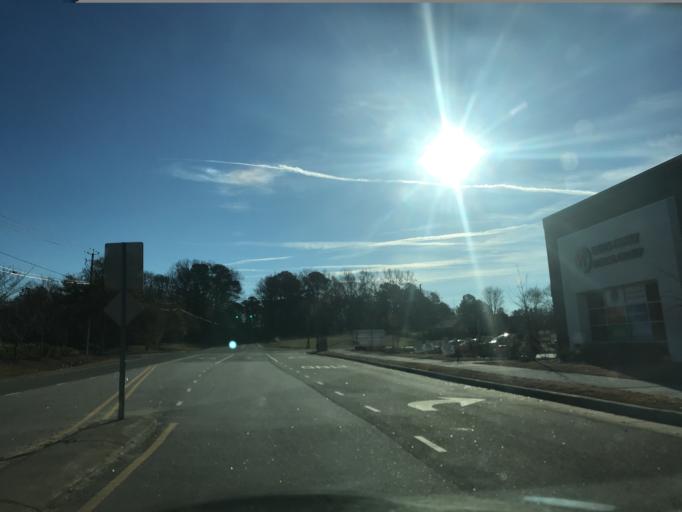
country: US
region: North Carolina
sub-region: Wake County
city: Cary
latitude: 35.9074
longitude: -78.7270
